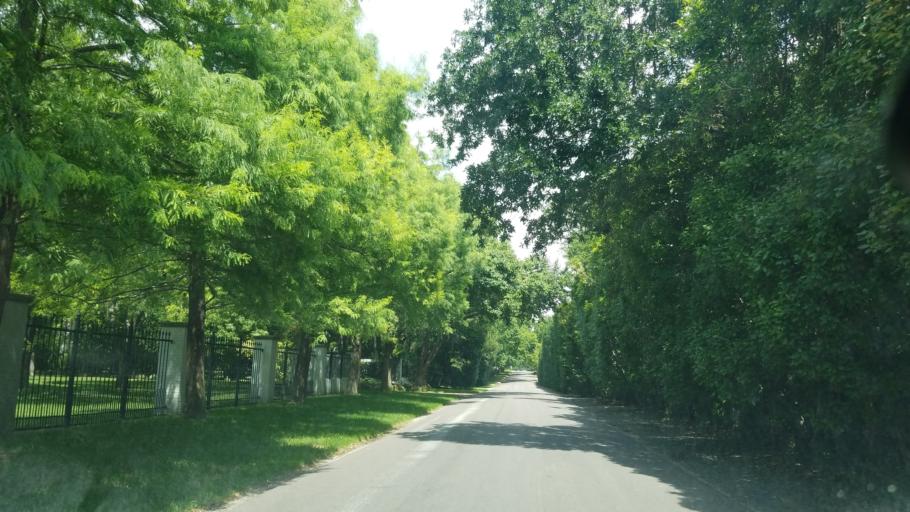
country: US
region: Texas
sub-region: Dallas County
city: University Park
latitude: 32.8707
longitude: -96.8083
